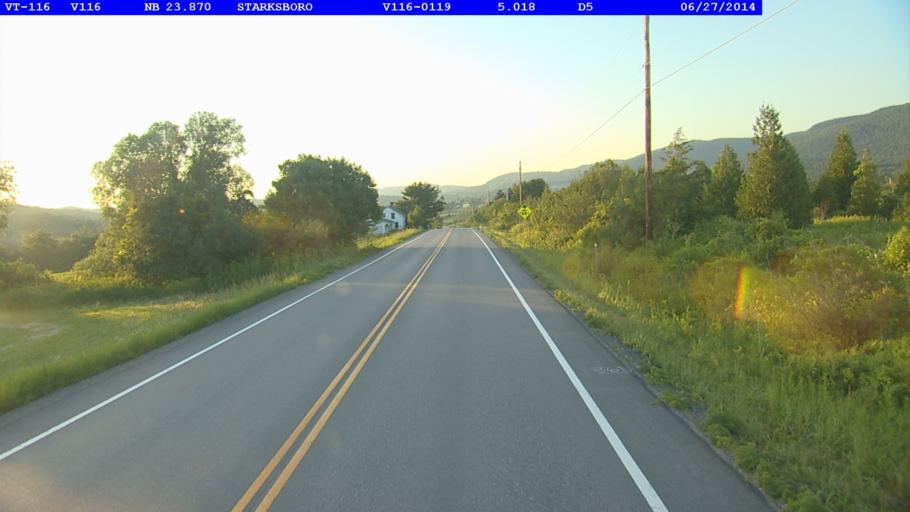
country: US
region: Vermont
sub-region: Chittenden County
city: Hinesburg
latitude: 44.2565
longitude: -73.0636
